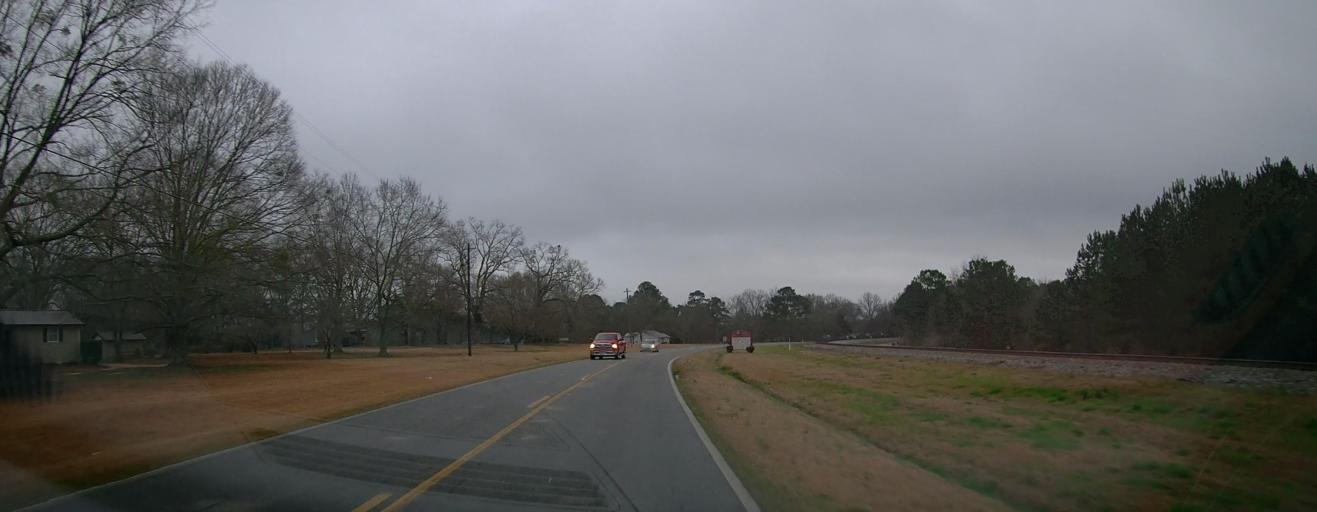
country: US
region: Georgia
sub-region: Lamar County
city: Barnesville
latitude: 33.1321
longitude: -84.1923
